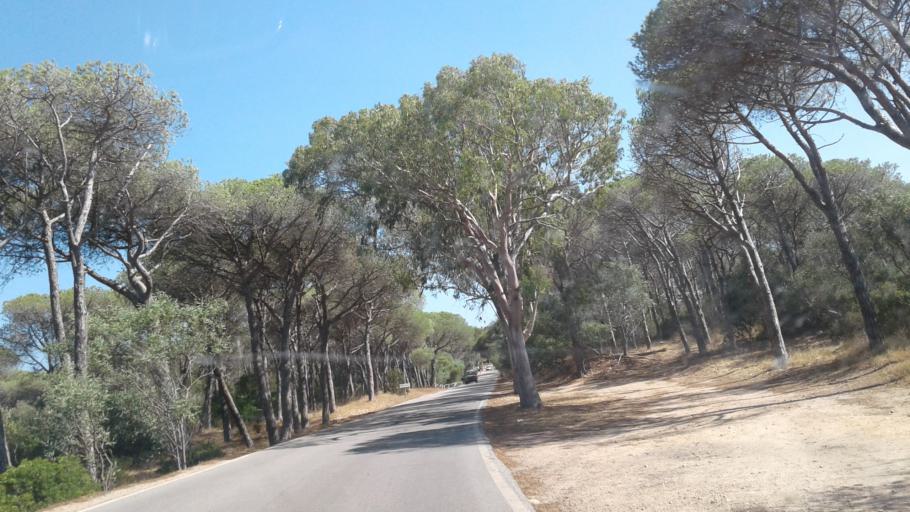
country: IT
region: Sardinia
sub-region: Provincia di Olbia-Tempio
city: La Maddalena
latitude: 41.2138
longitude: 9.4543
